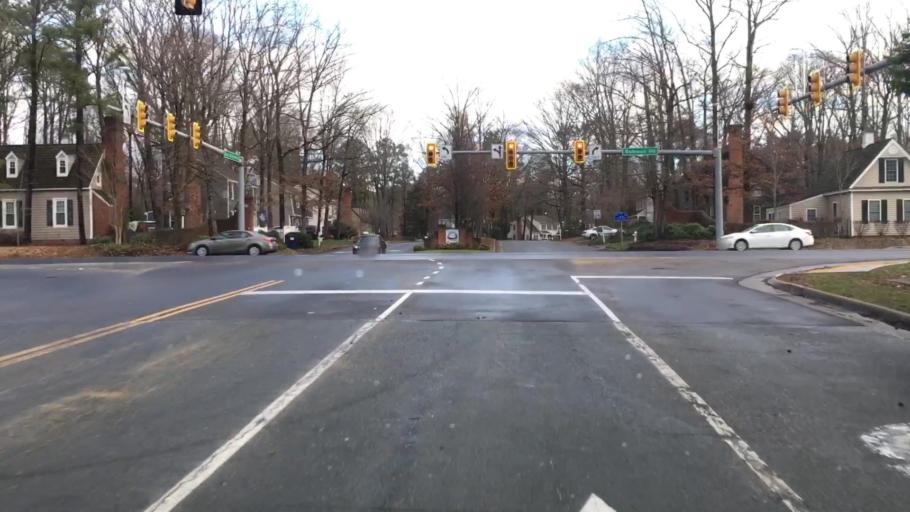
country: US
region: Virginia
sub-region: Chesterfield County
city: Bon Air
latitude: 37.5139
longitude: -77.5911
